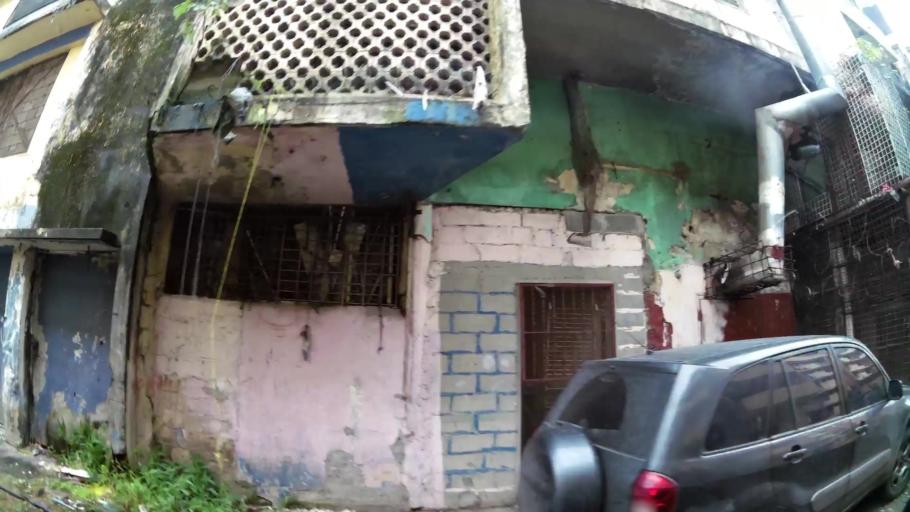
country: PA
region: Panama
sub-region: Distrito de Panama
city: Ancon
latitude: 8.9639
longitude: -79.5410
